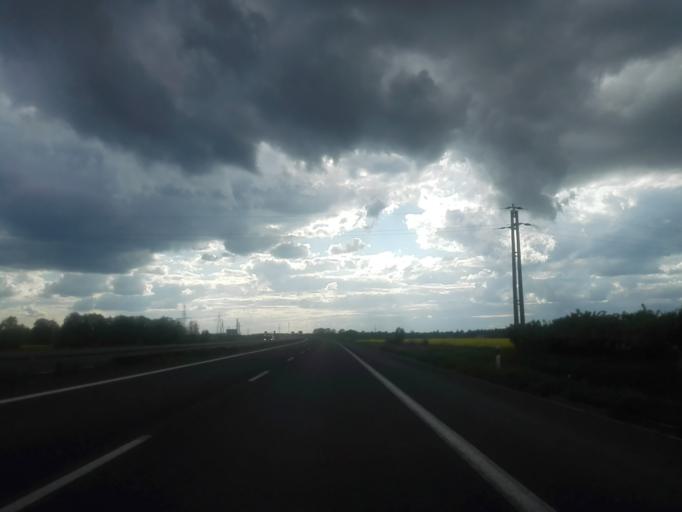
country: PL
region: Masovian Voivodeship
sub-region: Powiat ostrowski
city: Ostrow Mazowiecka
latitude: 52.8207
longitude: 21.9098
